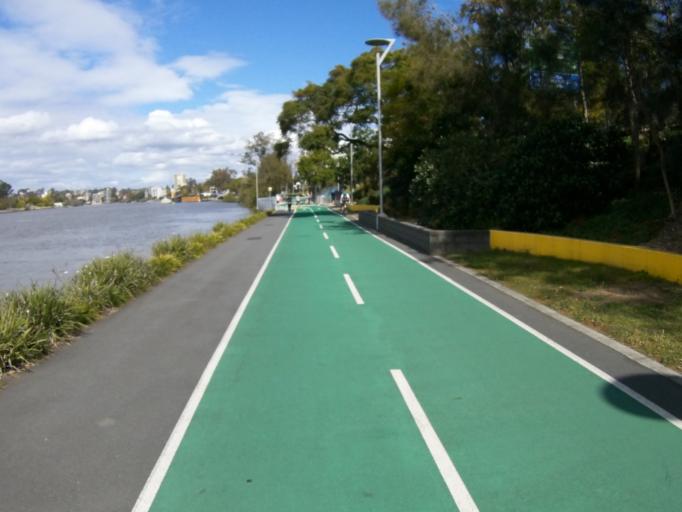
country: AU
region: Queensland
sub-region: Brisbane
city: Milton
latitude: -27.4789
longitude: 152.9994
